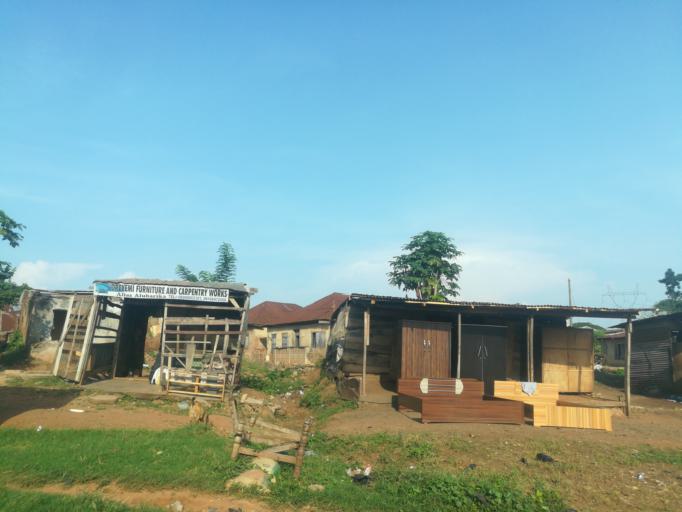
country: NG
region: Oyo
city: Moniya
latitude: 7.5204
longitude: 3.9122
